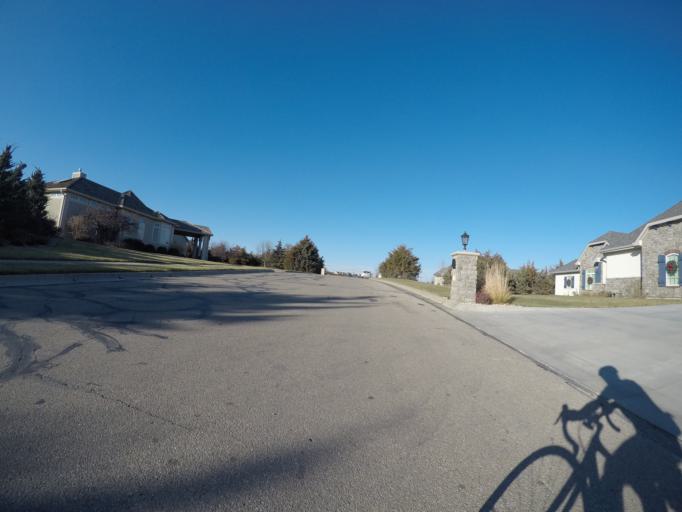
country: US
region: Kansas
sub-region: Riley County
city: Manhattan
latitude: 39.1941
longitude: -96.6389
